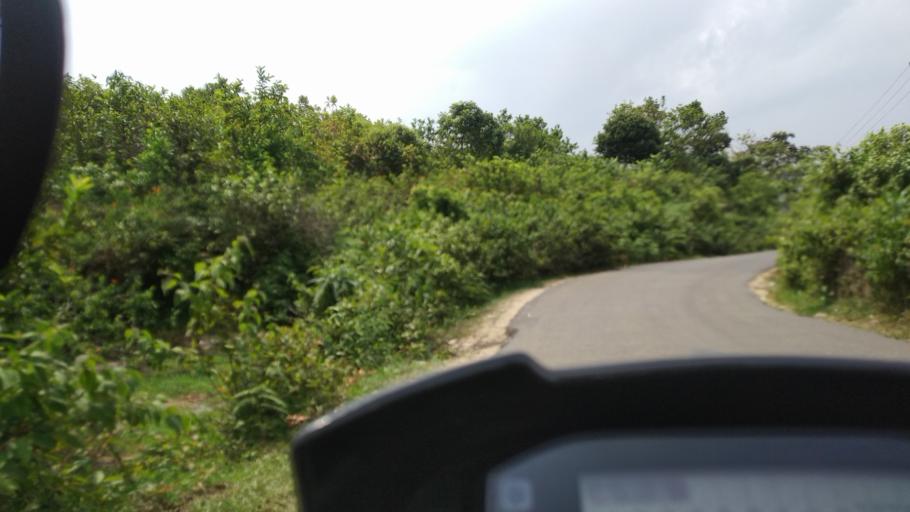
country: IN
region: Kerala
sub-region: Kottayam
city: Erattupetta
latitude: 9.6401
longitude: 76.9289
